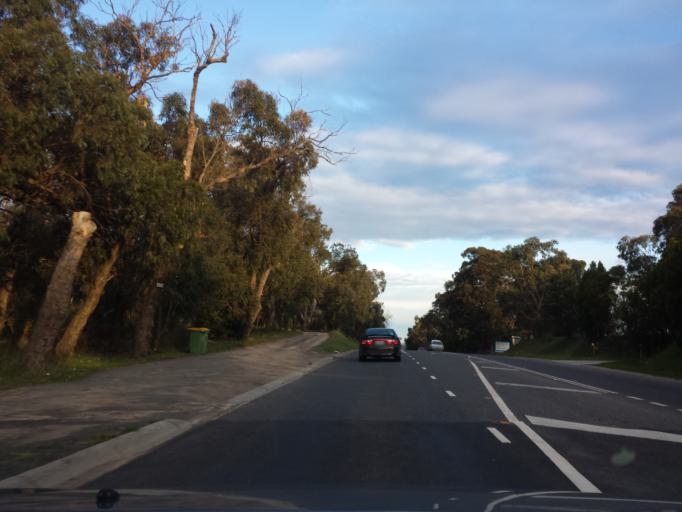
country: AU
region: Victoria
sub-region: Yarra Ranges
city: Belgrave South
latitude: -37.9413
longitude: 145.3190
